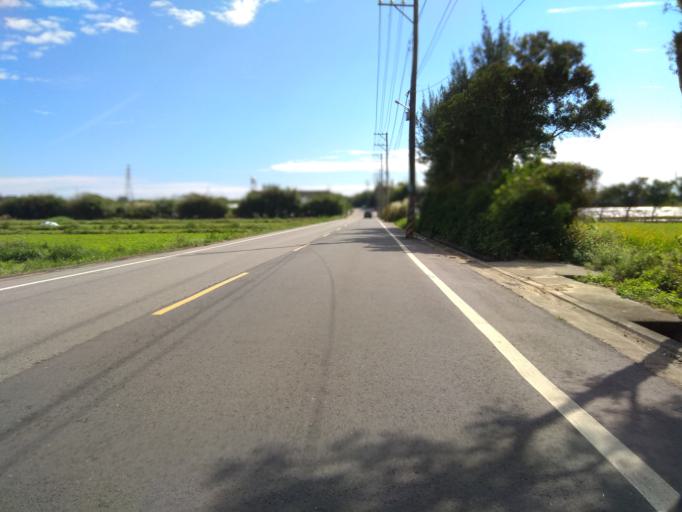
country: TW
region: Taiwan
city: Taoyuan City
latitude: 25.0419
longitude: 121.1239
